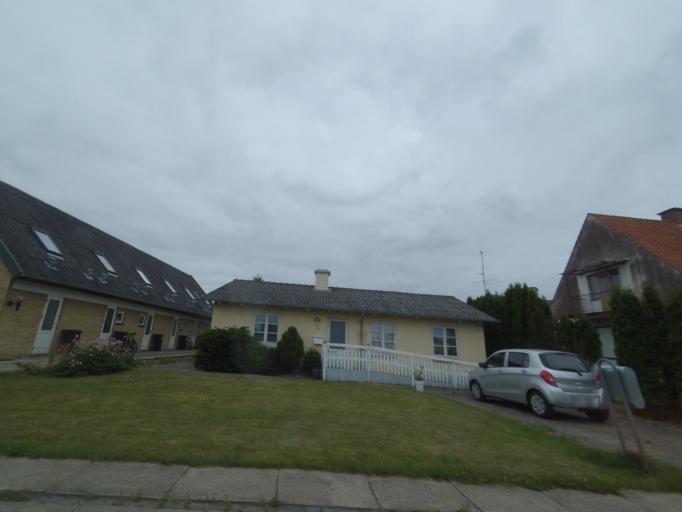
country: DK
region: South Denmark
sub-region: Nordfyns Kommune
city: Otterup
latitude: 55.5162
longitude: 10.4044
